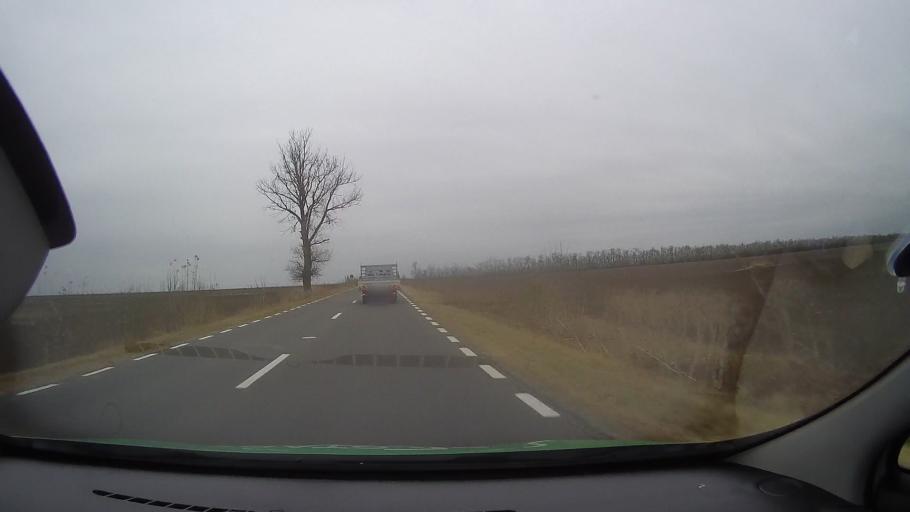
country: RO
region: Ialomita
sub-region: Comuna Gheorghe Lazar
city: Gheorghe Lazar
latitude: 44.6752
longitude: 27.4185
